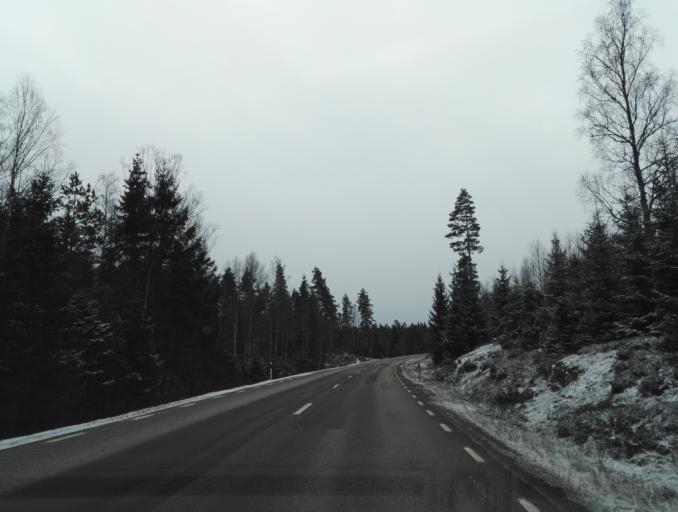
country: SE
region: Kalmar
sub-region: Hultsfreds Kommun
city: Virserum
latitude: 57.2768
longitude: 15.5704
